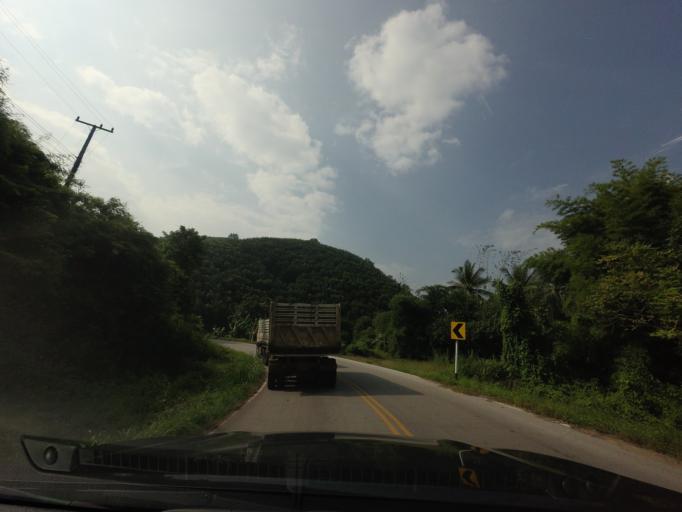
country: TH
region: Loei
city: Chiang Khan
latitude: 17.8334
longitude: 101.5634
